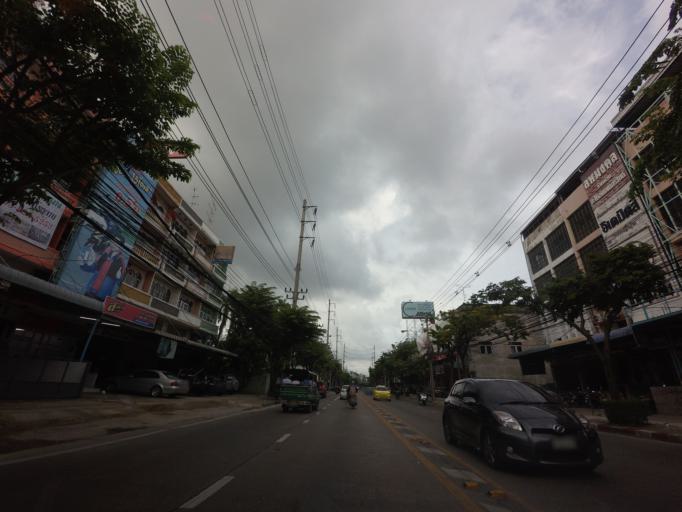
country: TH
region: Bangkok
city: Rat Burana
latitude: 13.6634
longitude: 100.5030
